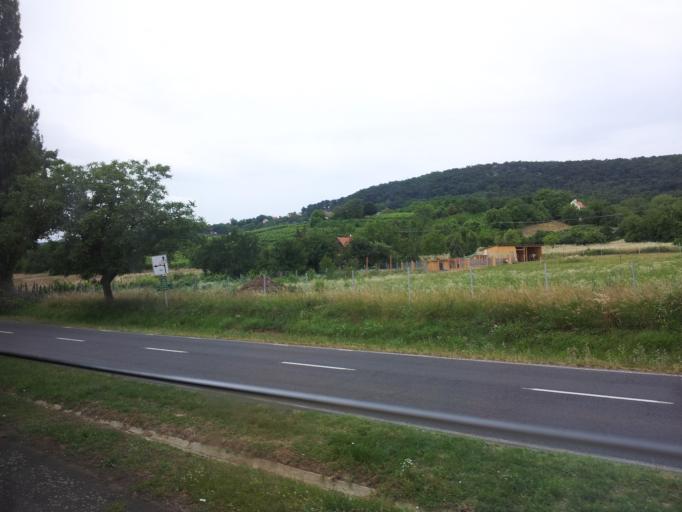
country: HU
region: Veszprem
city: Revfueloep
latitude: 46.8244
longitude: 17.5816
